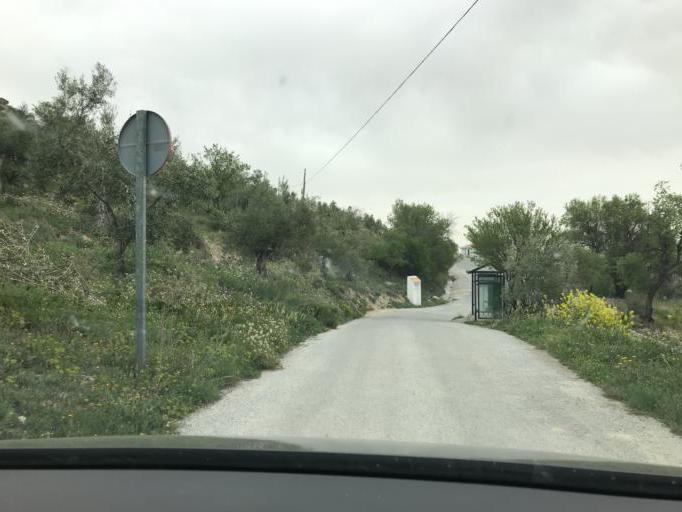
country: ES
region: Andalusia
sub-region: Provincia de Granada
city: Castril
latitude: 37.8034
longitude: -2.7714
